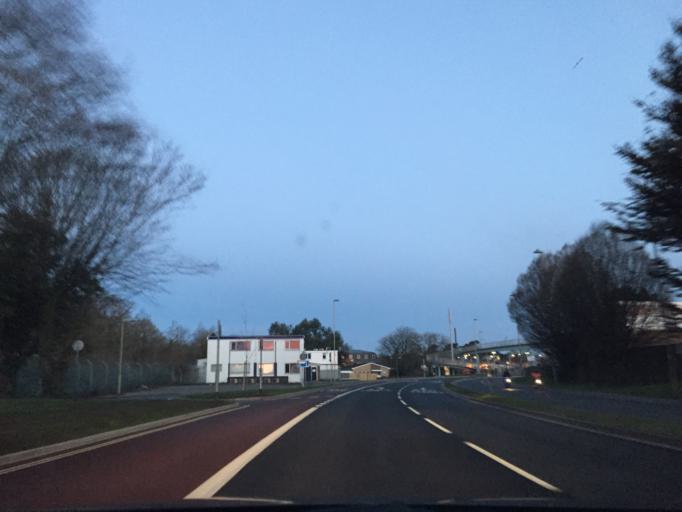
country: GB
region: England
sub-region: Hampshire
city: Fareham
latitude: 50.8517
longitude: -1.1882
